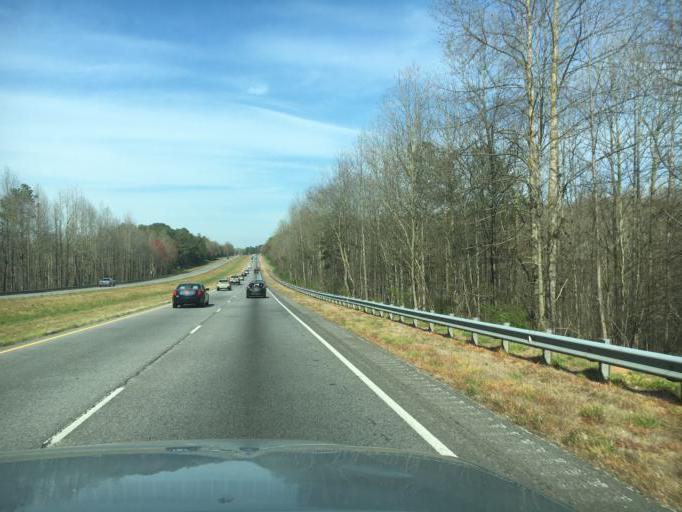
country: US
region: Georgia
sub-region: Hall County
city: Lula
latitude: 34.4293
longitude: -83.6422
